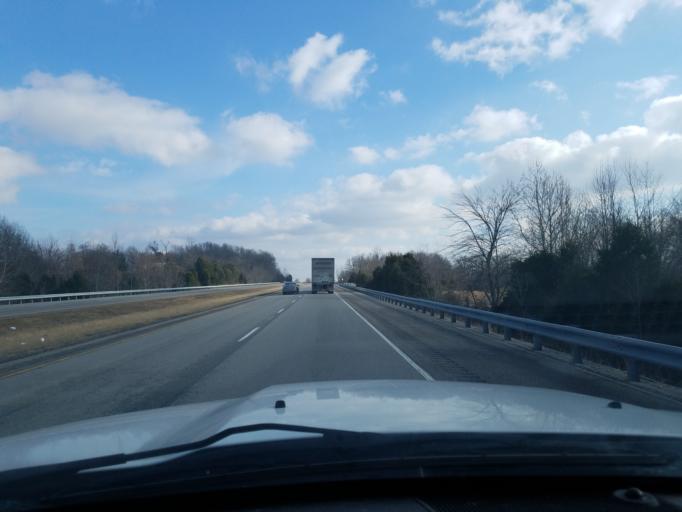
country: US
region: Kentucky
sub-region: Hardin County
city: Elizabethtown
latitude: 37.6336
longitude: -85.8274
